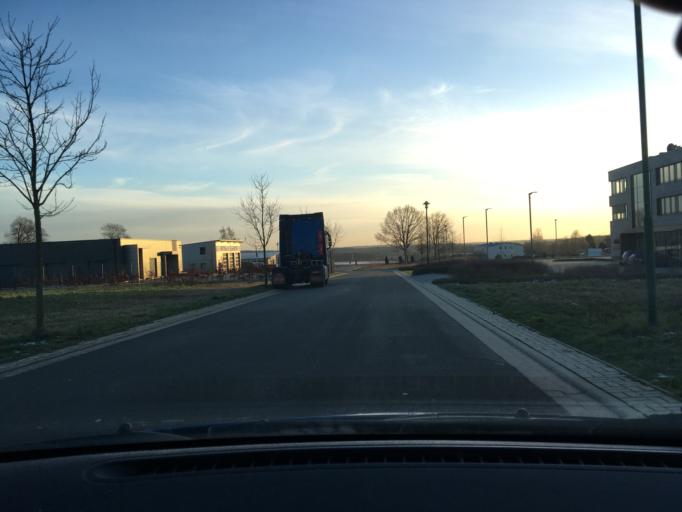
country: DE
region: Lower Saxony
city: Egestorf
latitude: 53.1959
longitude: 10.0741
